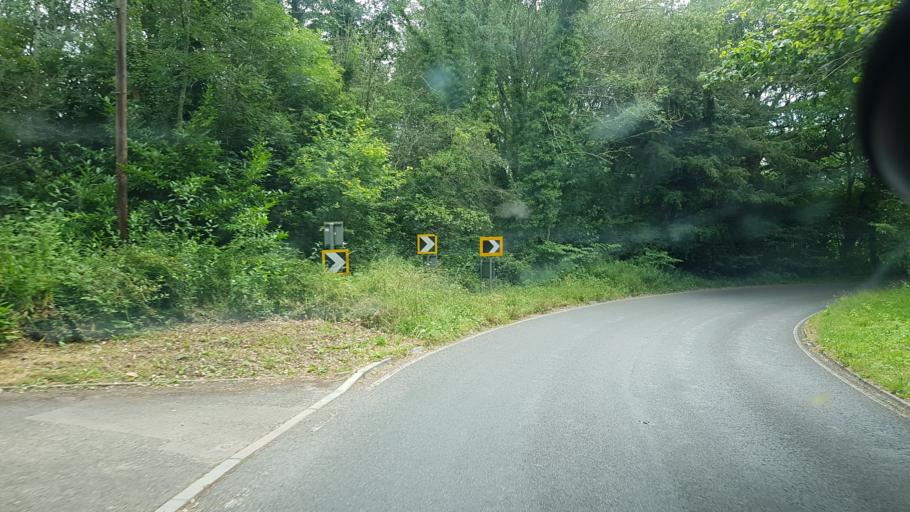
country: GB
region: England
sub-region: Surrey
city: Felbridge
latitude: 51.1174
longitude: -0.0329
